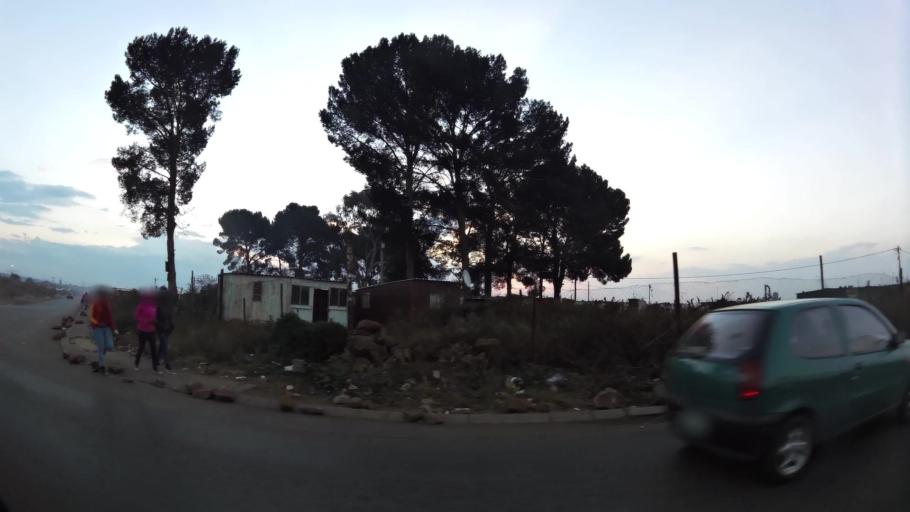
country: ZA
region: Gauteng
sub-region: City of Johannesburg Metropolitan Municipality
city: Orange Farm
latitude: -26.5553
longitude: 27.8799
